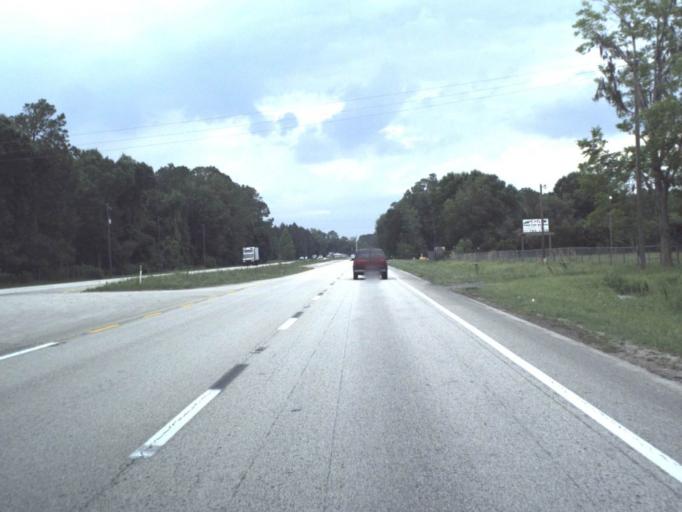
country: US
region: Florida
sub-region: Bradford County
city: Starke
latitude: 30.0663
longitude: -82.0660
